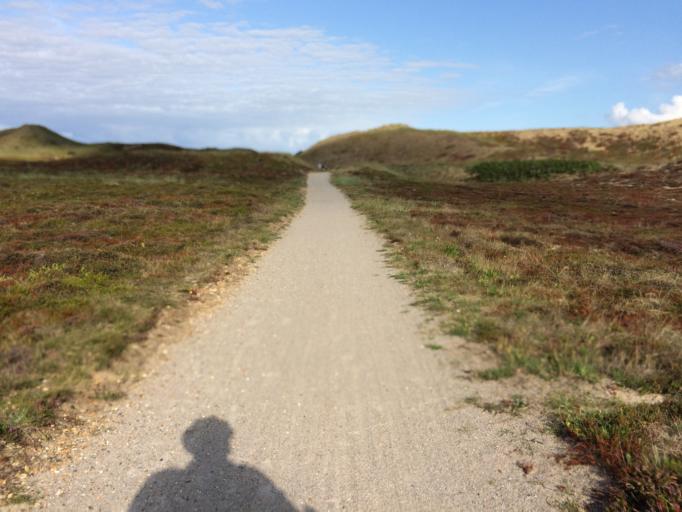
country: DK
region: Central Jutland
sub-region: Ringkobing-Skjern Kommune
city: Hvide Sande
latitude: 55.8944
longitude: 8.1671
